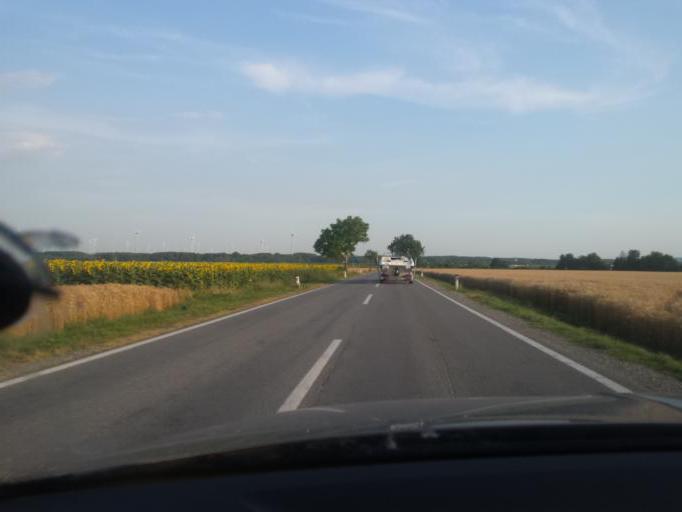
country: AT
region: Lower Austria
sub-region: Politischer Bezirk Bruck an der Leitha
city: Rohrau
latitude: 48.0889
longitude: 16.8624
